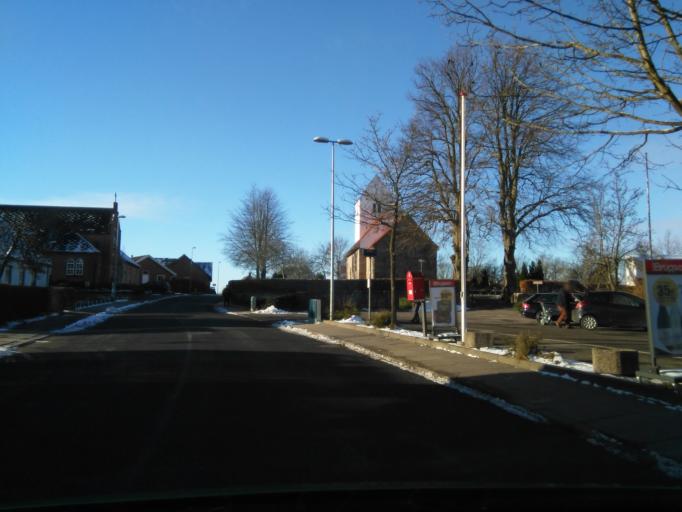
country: DK
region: Central Jutland
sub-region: Skanderborg Kommune
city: Skovby
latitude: 56.1171
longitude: 9.9552
